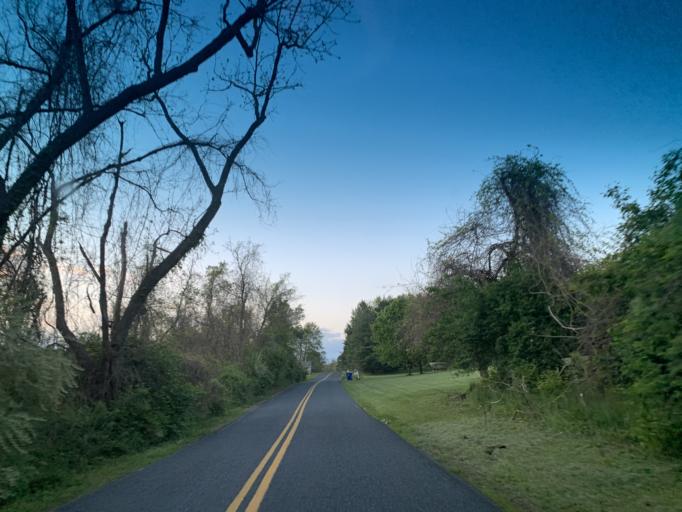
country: US
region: Maryland
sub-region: Harford County
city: Bel Air South
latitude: 39.5382
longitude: -76.2762
